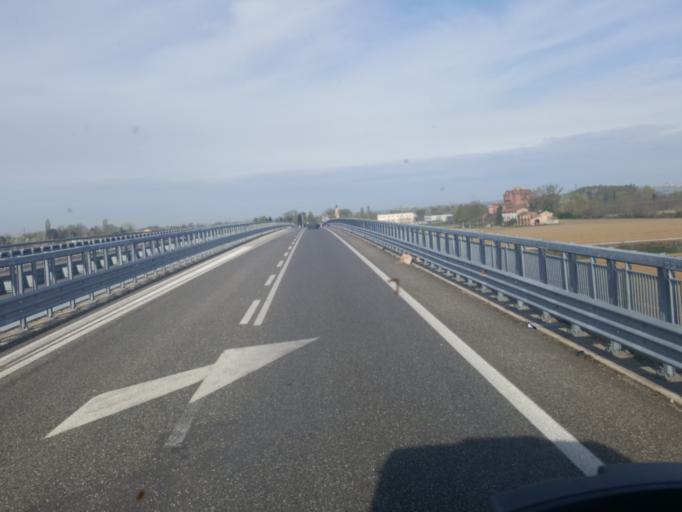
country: IT
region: Piedmont
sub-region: Provincia di Alessandria
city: Alessandria
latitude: 44.9348
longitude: 8.5927
